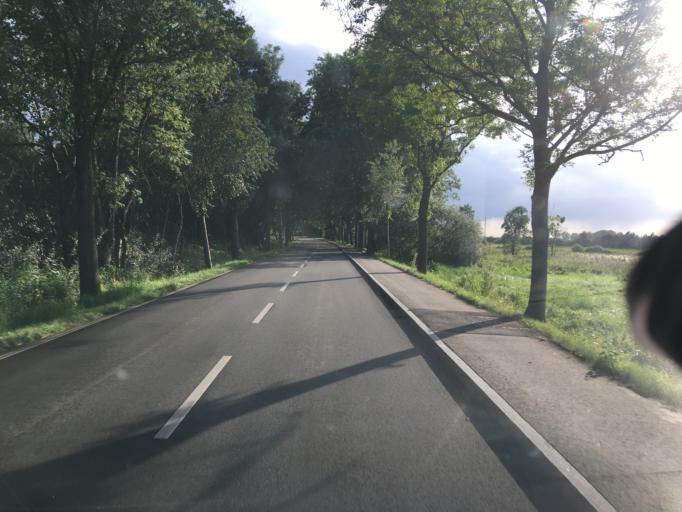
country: DE
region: Lower Saxony
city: Neu Wulmstorf
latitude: 53.4904
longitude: 9.8712
